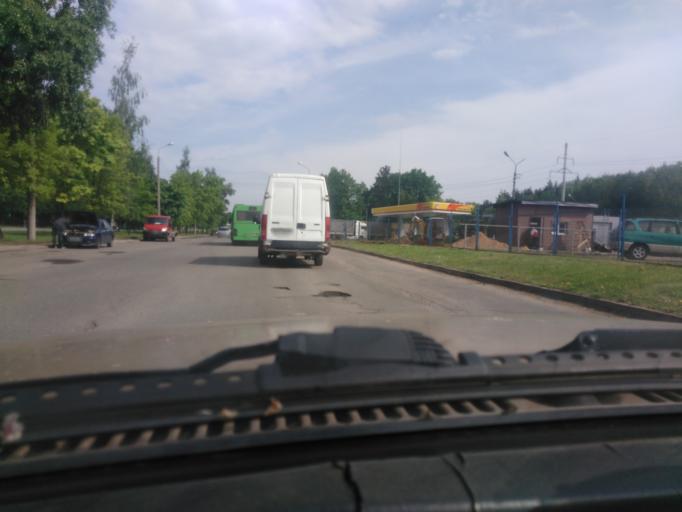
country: BY
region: Mogilev
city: Mahilyow
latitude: 53.9478
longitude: 30.3529
